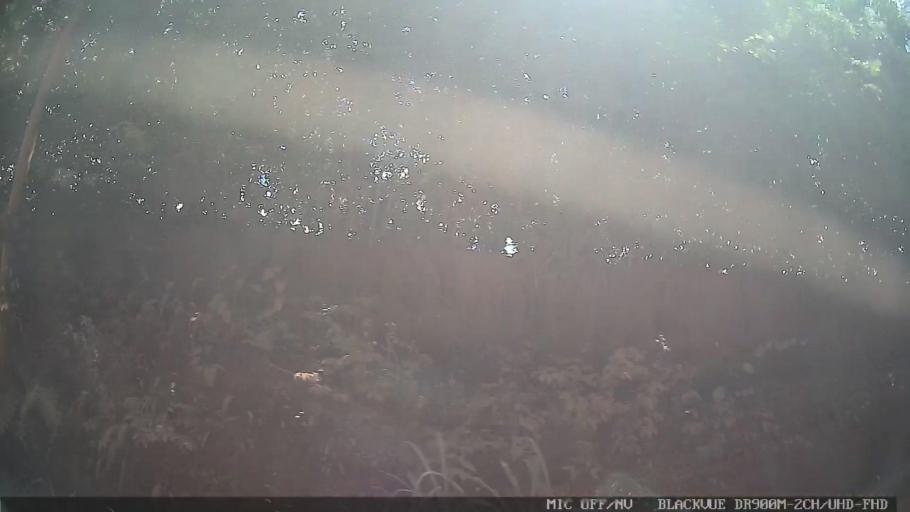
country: BR
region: Sao Paulo
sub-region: Atibaia
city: Atibaia
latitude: -23.1272
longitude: -46.6346
